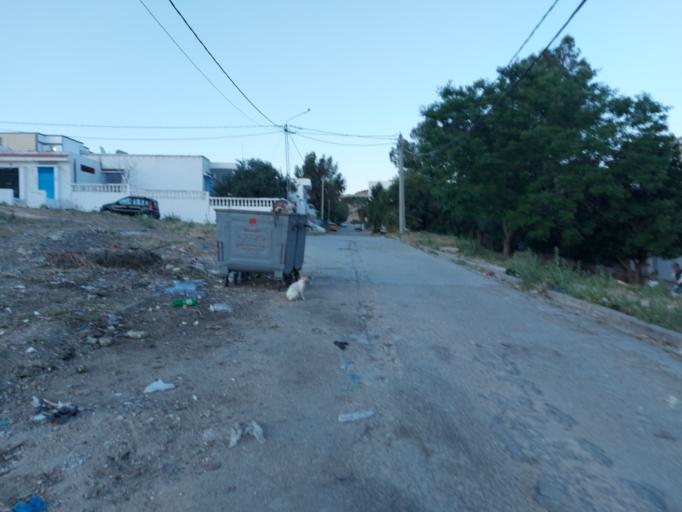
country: TN
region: Kef
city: El Kef
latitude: 36.1808
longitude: 8.7289
